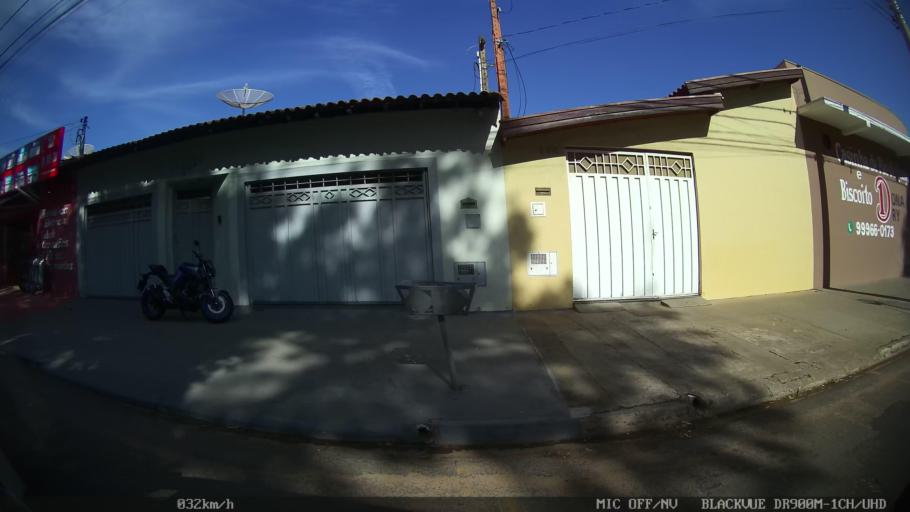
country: BR
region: Sao Paulo
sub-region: Franca
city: Franca
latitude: -20.5070
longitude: -47.4199
